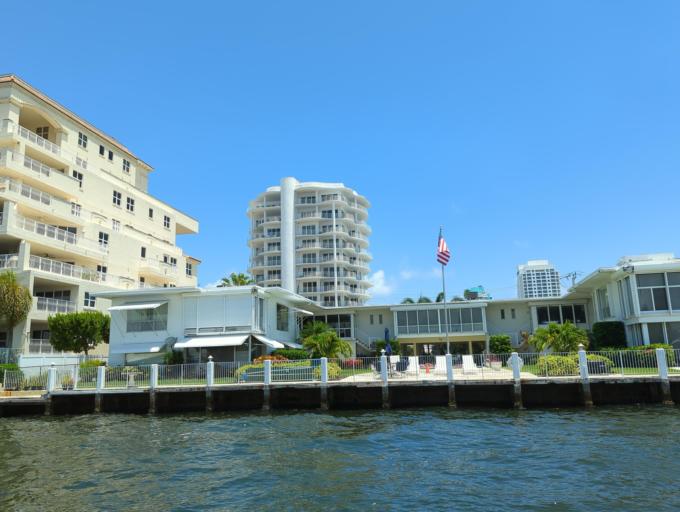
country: US
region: Florida
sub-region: Broward County
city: Sunrise
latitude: 26.1315
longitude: -80.1097
